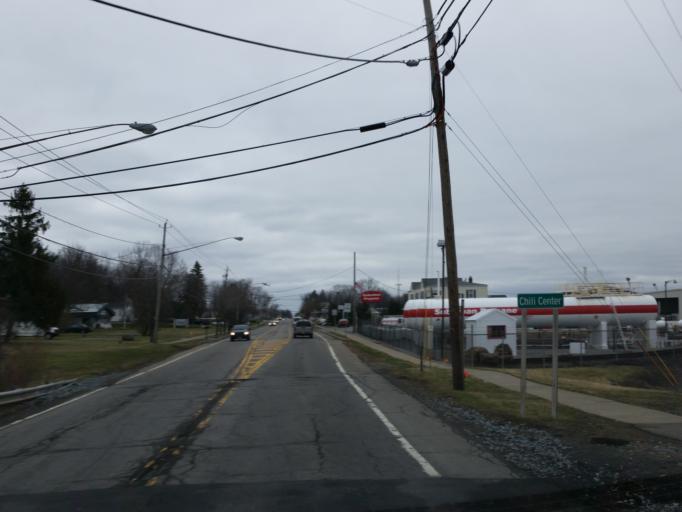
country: US
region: New York
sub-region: Monroe County
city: Scottsville
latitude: 43.1010
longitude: -77.7587
